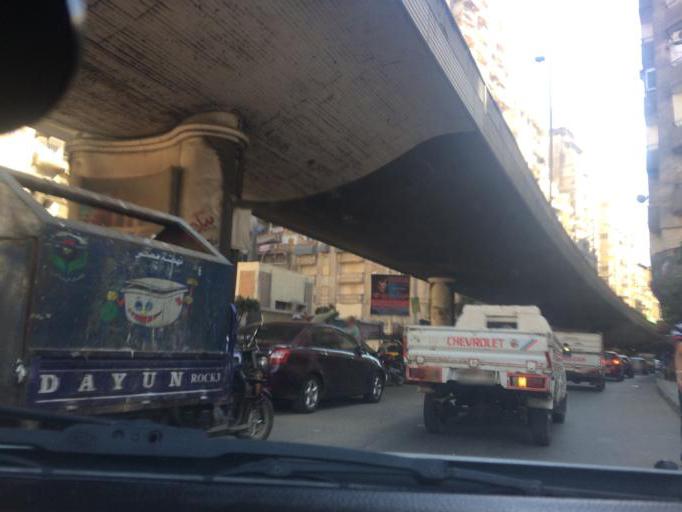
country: EG
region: Alexandria
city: Alexandria
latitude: 31.2675
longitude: 30.0000
